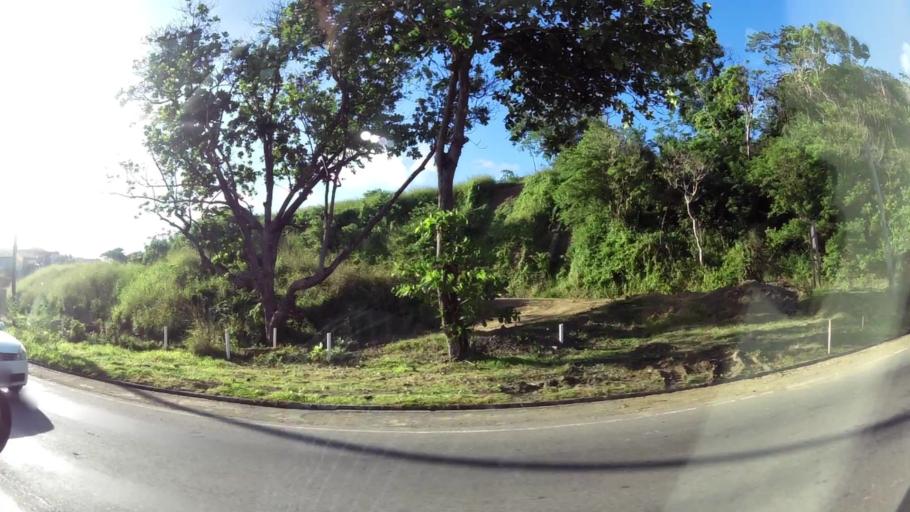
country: TT
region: Tobago
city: Scarborough
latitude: 11.1911
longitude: -60.6950
